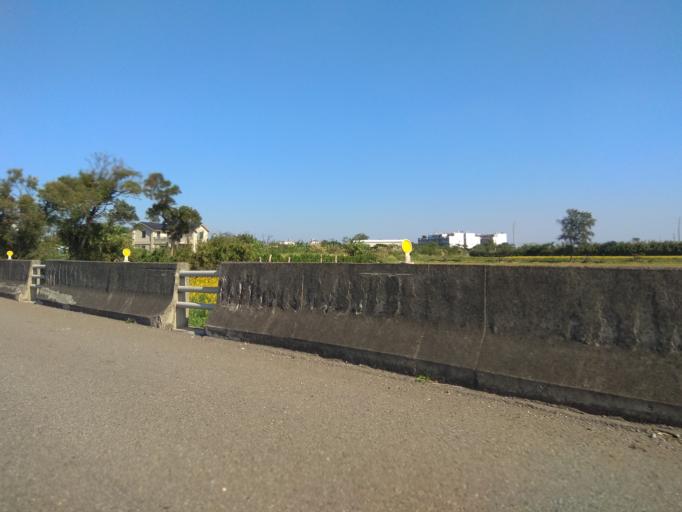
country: TW
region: Taiwan
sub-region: Hsinchu
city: Zhubei
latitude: 24.9913
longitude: 121.0333
